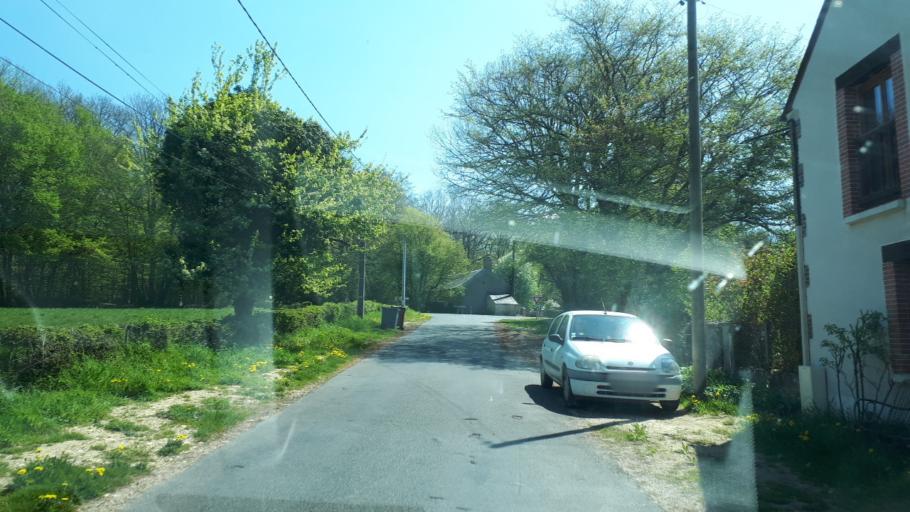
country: FR
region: Centre
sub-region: Departement du Cher
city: Henrichemont
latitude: 47.2979
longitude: 2.5791
